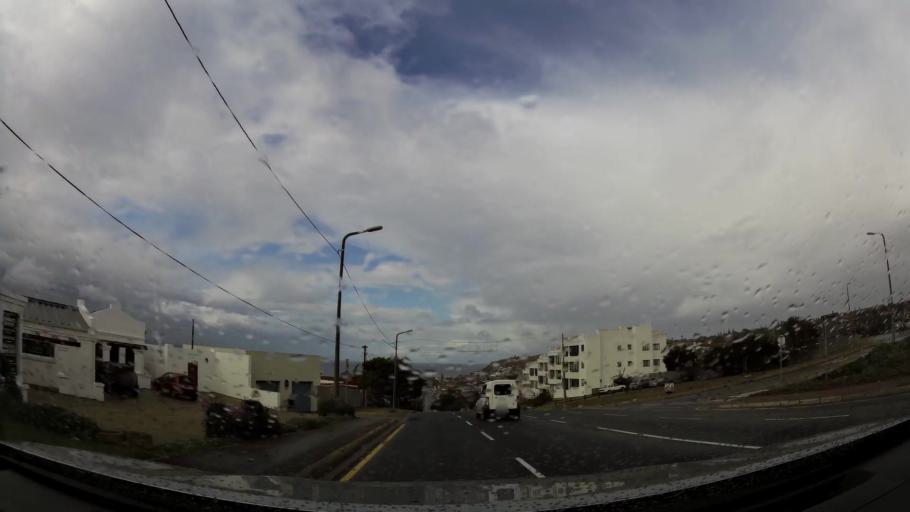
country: ZA
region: Western Cape
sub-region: Eden District Municipality
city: Mossel Bay
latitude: -34.1823
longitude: 22.1365
